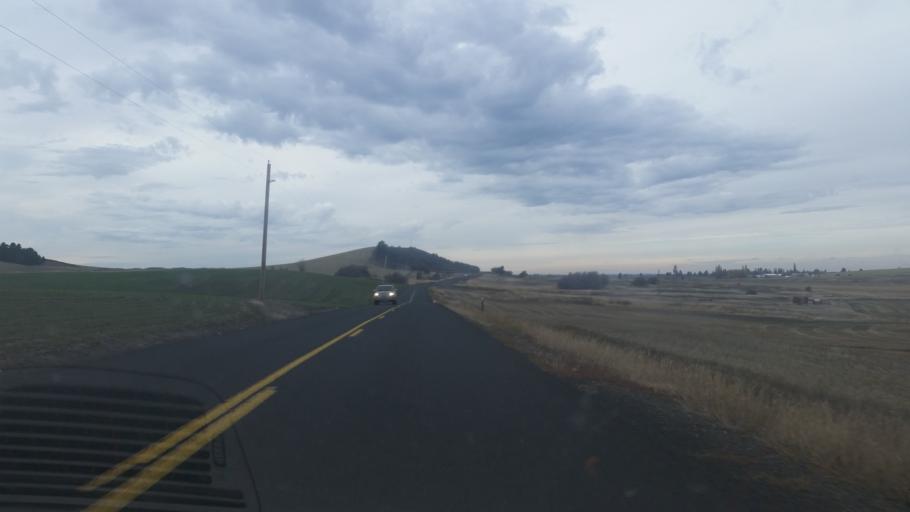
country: US
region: Washington
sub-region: Spokane County
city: Cheney
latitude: 47.3907
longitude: -117.4412
